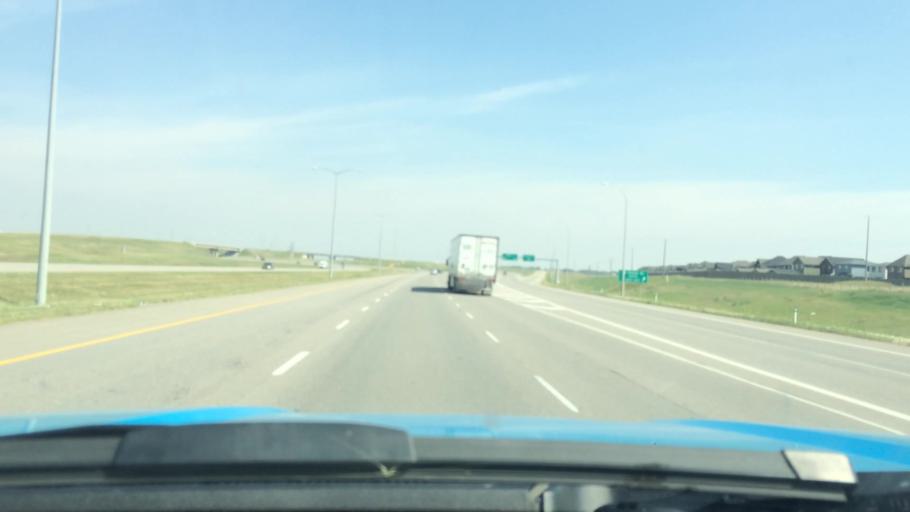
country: CA
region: Alberta
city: Chestermere
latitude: 50.9066
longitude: -113.9234
